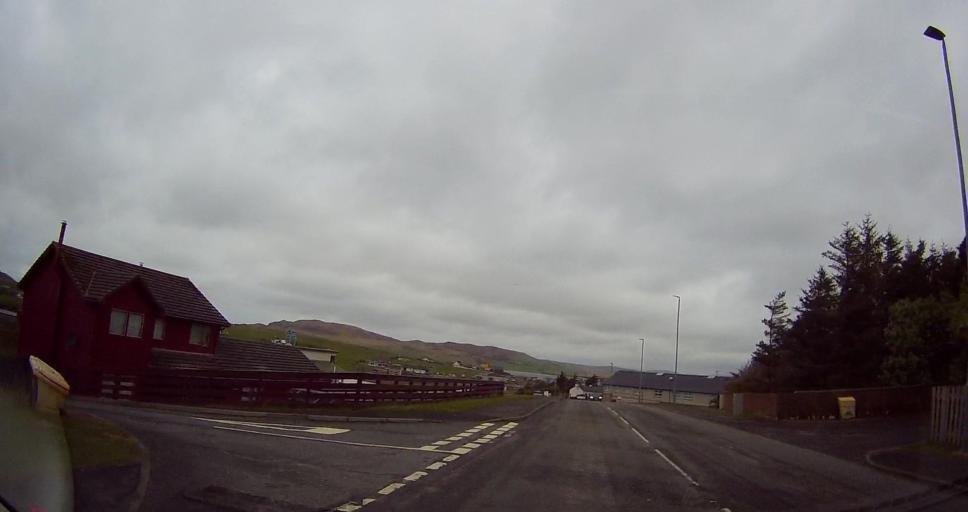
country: GB
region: Scotland
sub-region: Shetland Islands
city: Lerwick
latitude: 60.3924
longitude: -1.3497
